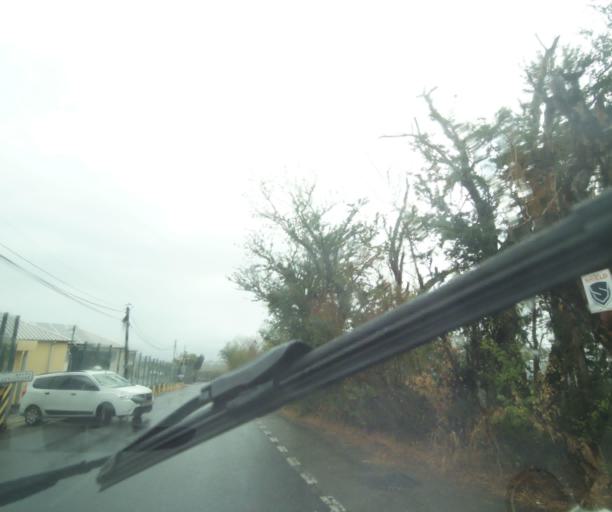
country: RE
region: Reunion
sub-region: Reunion
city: Le Port
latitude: -20.9753
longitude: 55.3005
